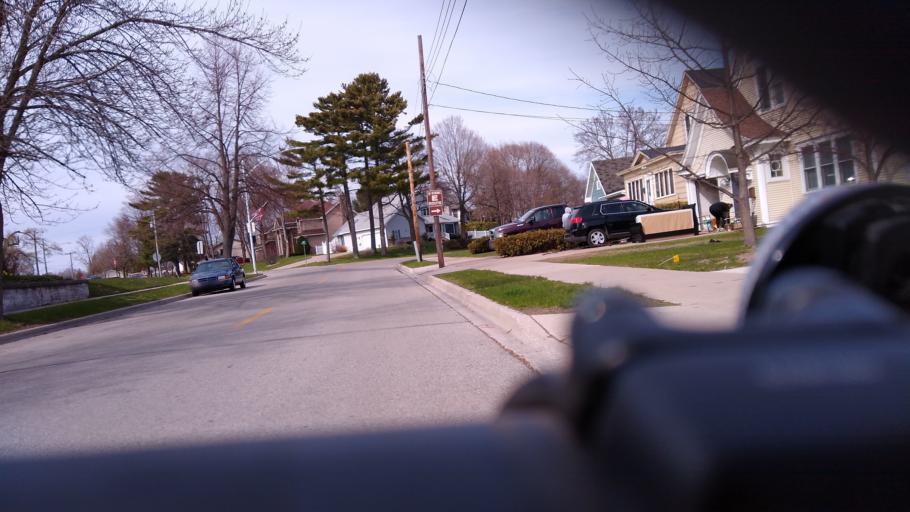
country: US
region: Michigan
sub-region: Delta County
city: Escanaba
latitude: 45.7367
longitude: -87.0594
